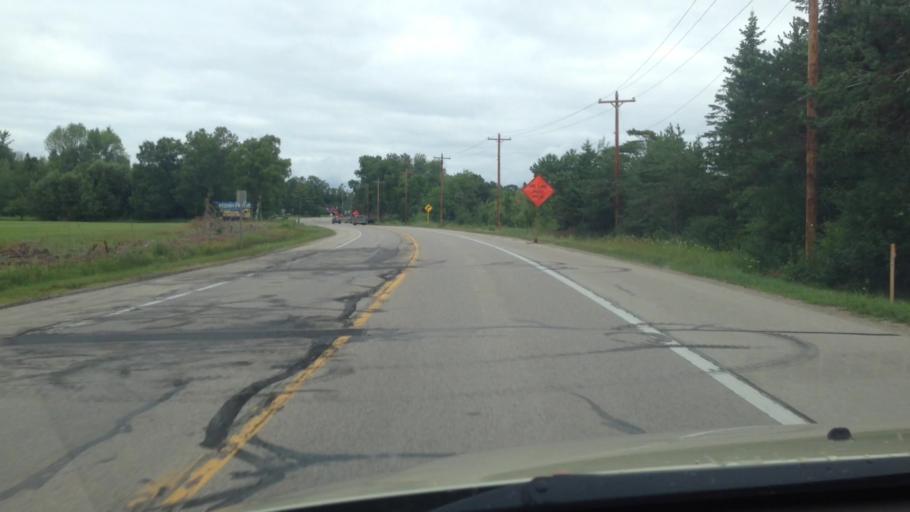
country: US
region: Michigan
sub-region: Delta County
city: Escanaba
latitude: 45.6938
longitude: -87.1005
